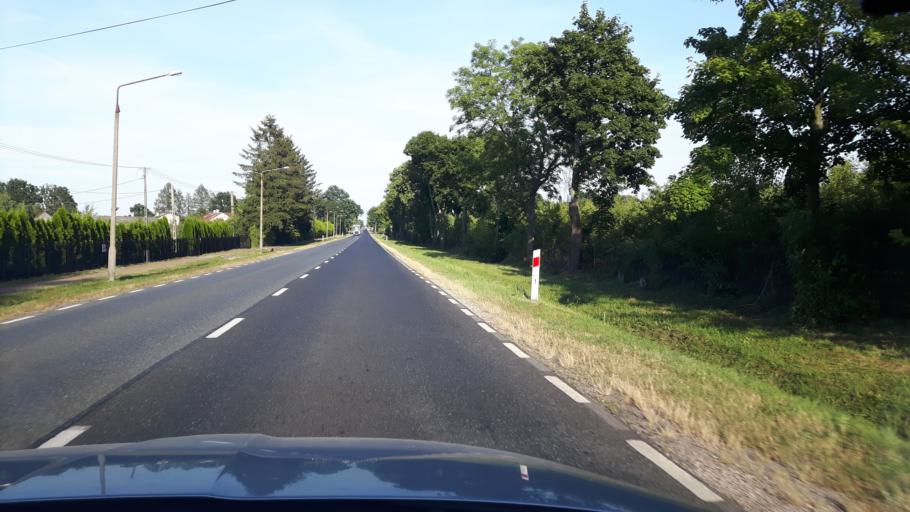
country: PL
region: Masovian Voivodeship
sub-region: Powiat legionowski
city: Wieliszew
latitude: 52.5052
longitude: 20.9951
